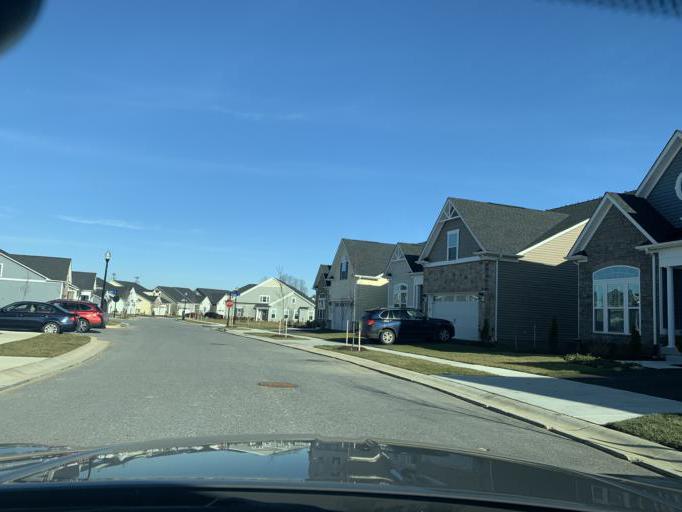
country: US
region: Maryland
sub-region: Anne Arundel County
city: Crofton
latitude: 39.0263
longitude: -76.7295
